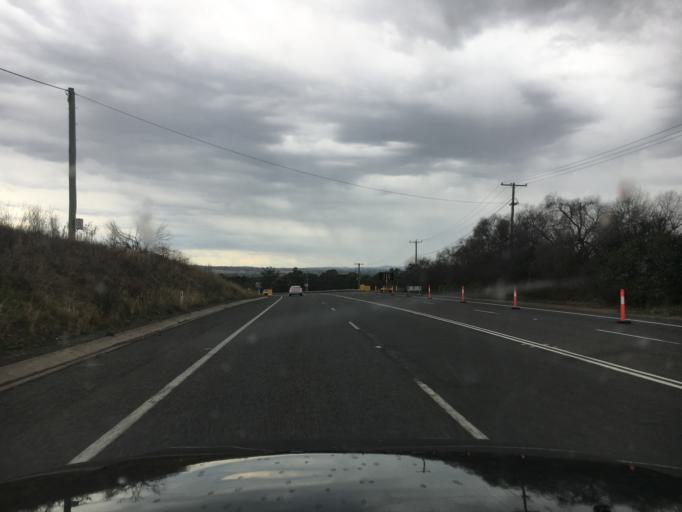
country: AU
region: New South Wales
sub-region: Muswellbrook
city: Muswellbrook
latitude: -32.2055
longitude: 150.8934
